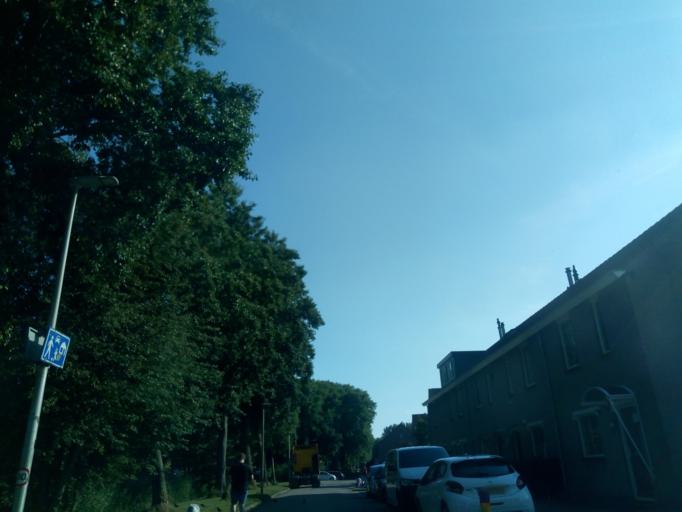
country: NL
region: South Holland
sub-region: Gemeente Alphen aan den Rijn
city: Alphen aan den Rijn
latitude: 52.1553
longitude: 4.6544
